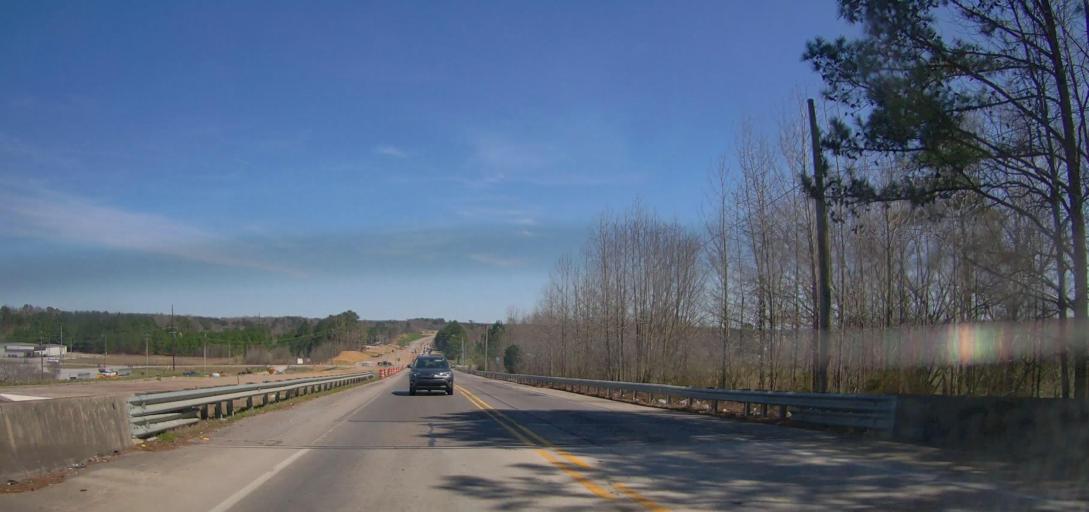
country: US
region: Alabama
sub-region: Cullman County
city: Cullman
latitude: 34.2061
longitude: -86.8501
